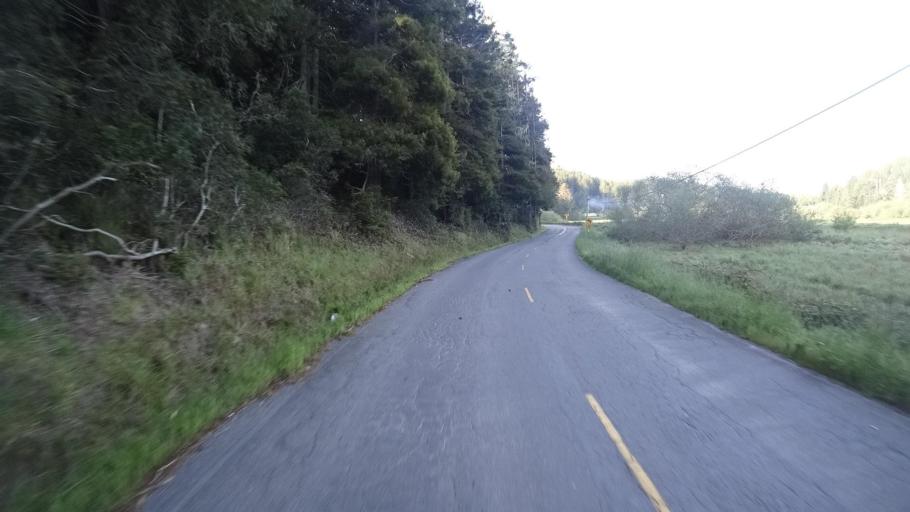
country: US
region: California
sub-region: Humboldt County
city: Myrtletown
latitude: 40.7793
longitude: -124.1182
